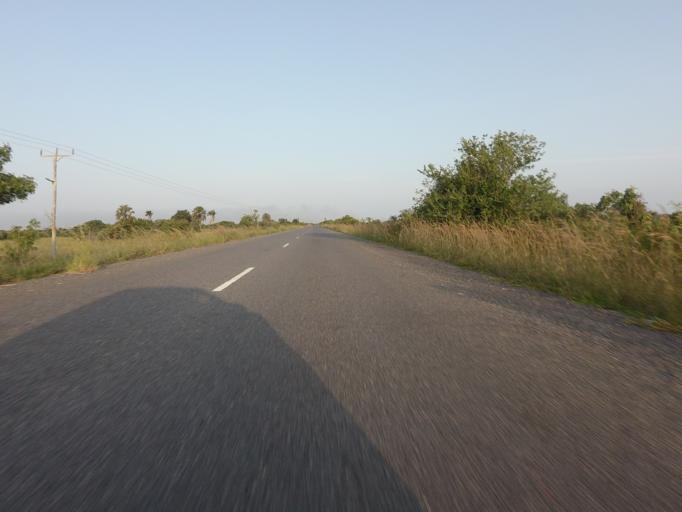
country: GH
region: Volta
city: Anloga
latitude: 5.8523
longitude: 0.7716
